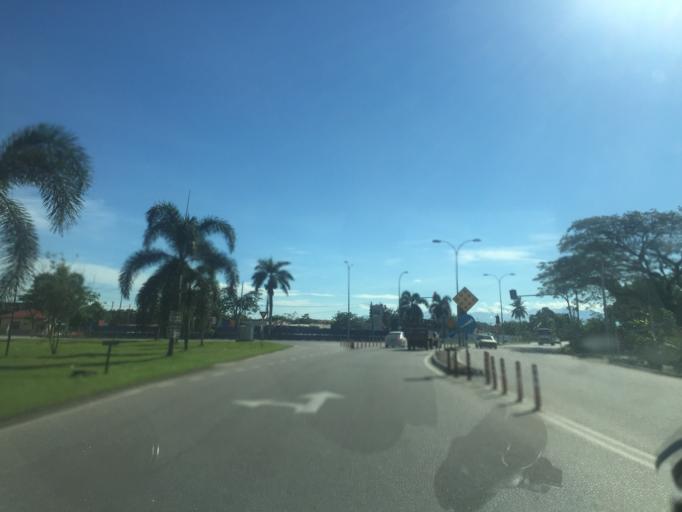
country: MY
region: Penang
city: Tasek Glugor
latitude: 5.5155
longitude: 100.5463
